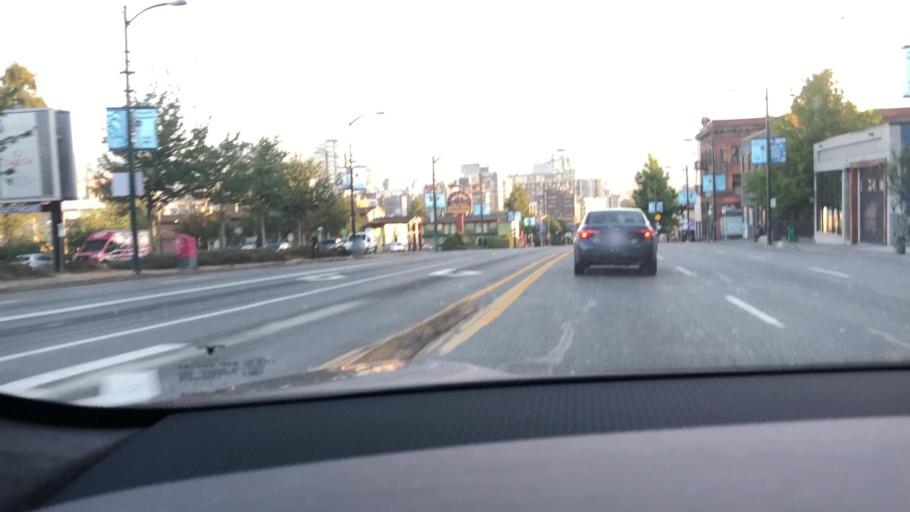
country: CA
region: British Columbia
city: Vancouver
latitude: 49.2647
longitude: -123.1010
